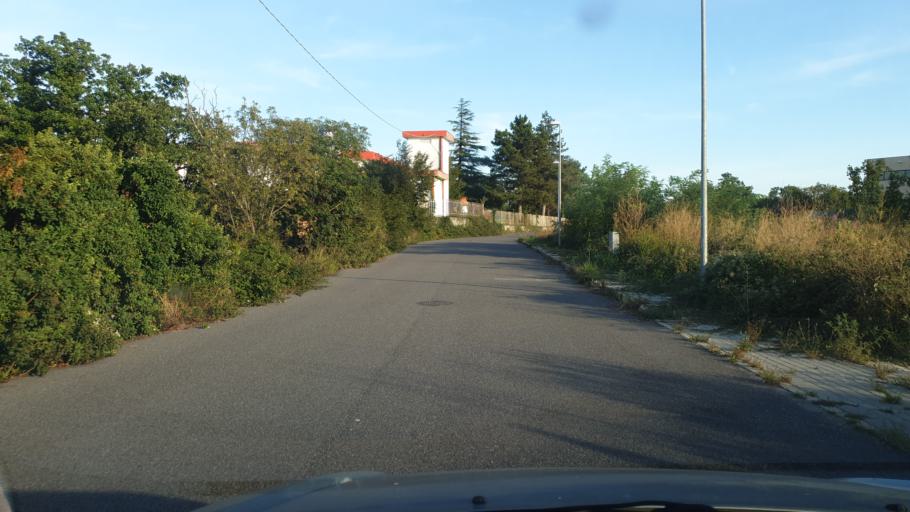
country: IT
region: Friuli Venezia Giulia
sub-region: Provincia di Trieste
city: Prosecco-Contovello
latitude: 45.7144
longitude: 13.7396
